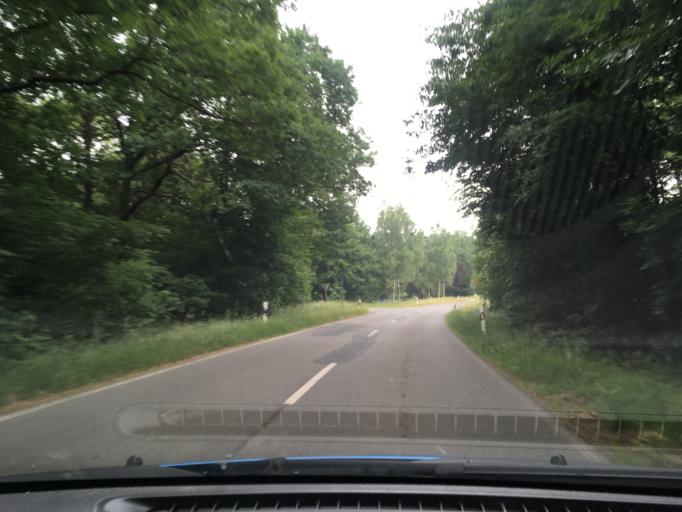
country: DE
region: Lower Saxony
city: Zernien
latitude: 53.0782
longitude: 10.8841
